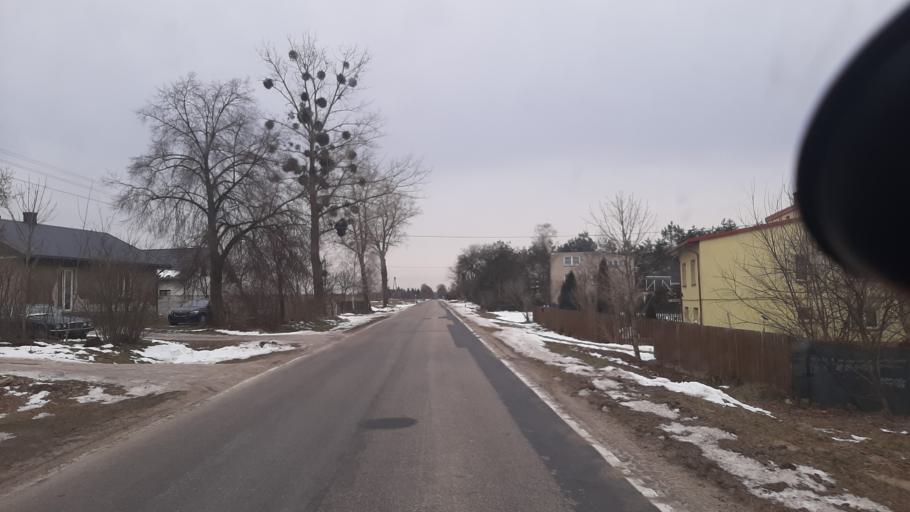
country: PL
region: Lublin Voivodeship
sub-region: Powiat lubartowski
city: Kamionka
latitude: 51.4664
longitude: 22.4199
